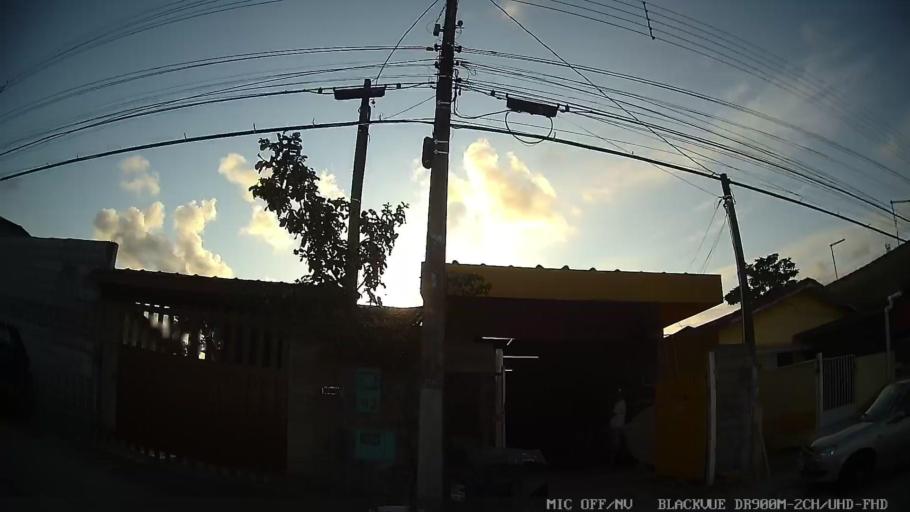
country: BR
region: Sao Paulo
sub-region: Itanhaem
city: Itanhaem
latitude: -24.1804
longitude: -46.8241
